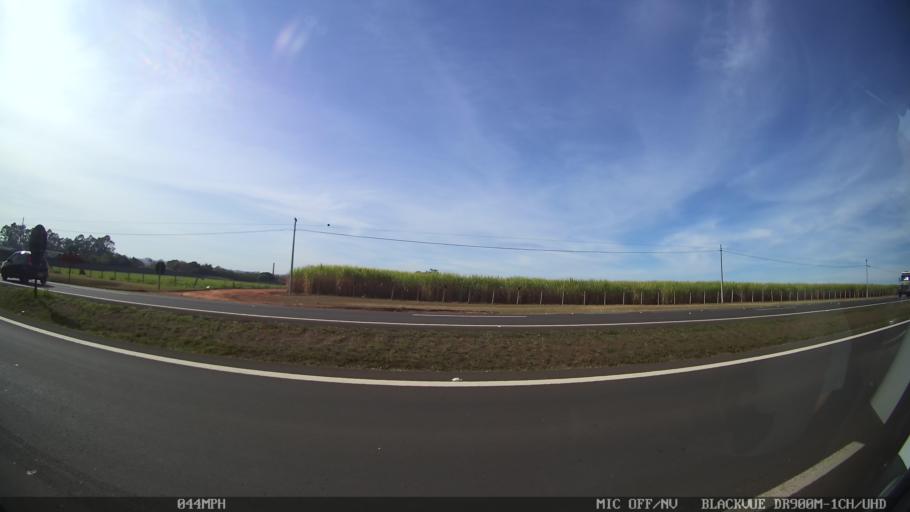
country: BR
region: Sao Paulo
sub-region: Piracicaba
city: Piracicaba
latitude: -22.7781
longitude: -47.6512
